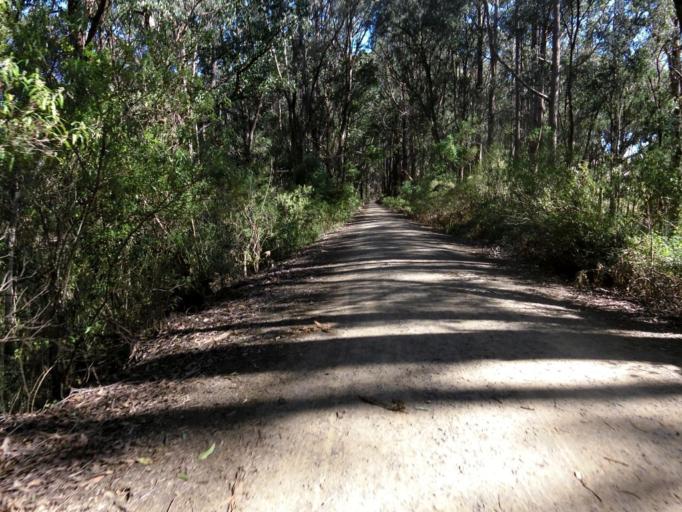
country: AU
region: Victoria
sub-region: Latrobe
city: Moe
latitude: -38.3962
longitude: 146.1765
